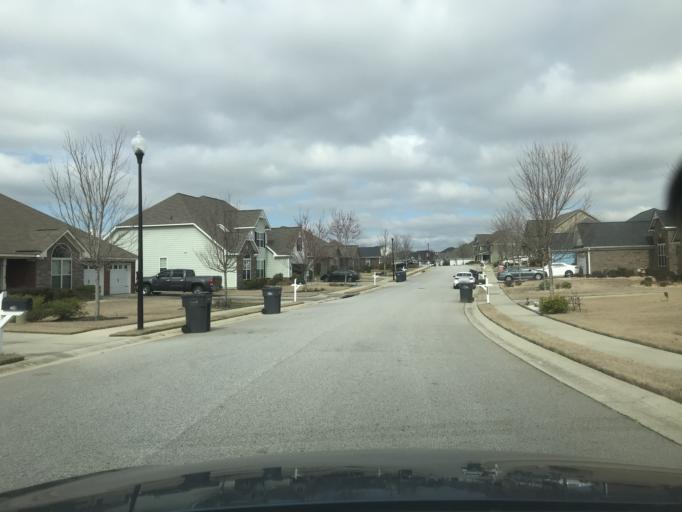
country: US
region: Georgia
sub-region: Columbia County
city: Grovetown
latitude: 33.4391
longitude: -82.1507
